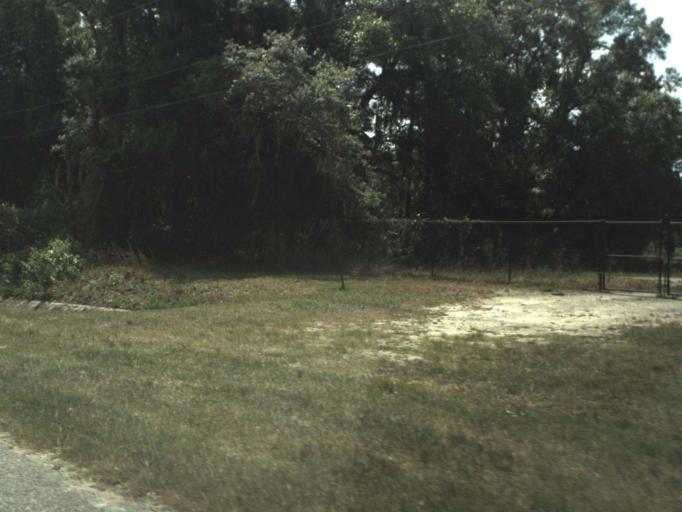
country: US
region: Florida
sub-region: Volusia County
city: North DeLand
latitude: 29.0548
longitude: -81.2936
